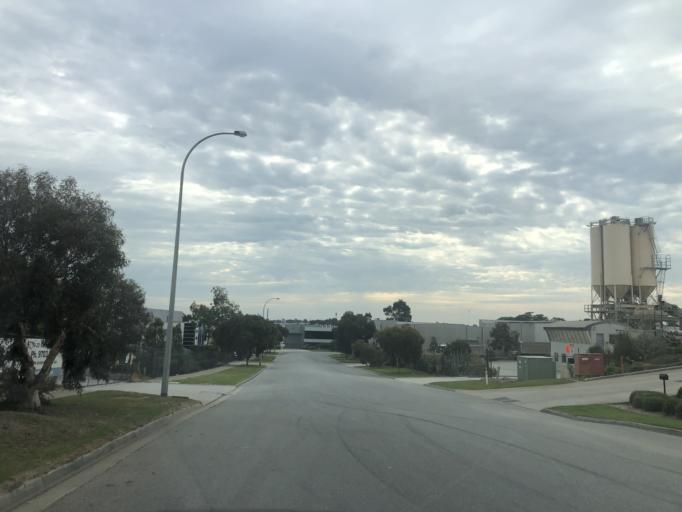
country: AU
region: Victoria
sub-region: Casey
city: Hallam
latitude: -38.0136
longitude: 145.2598
